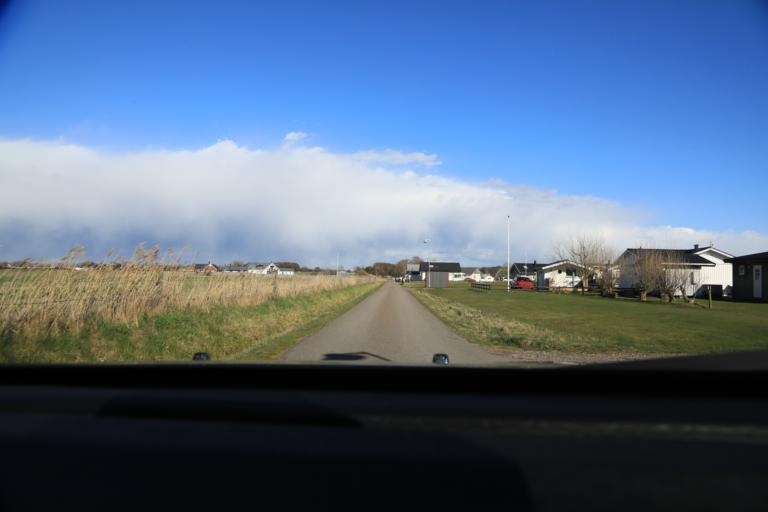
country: SE
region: Halland
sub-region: Varbergs Kommun
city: Traslovslage
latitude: 57.0709
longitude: 12.2726
